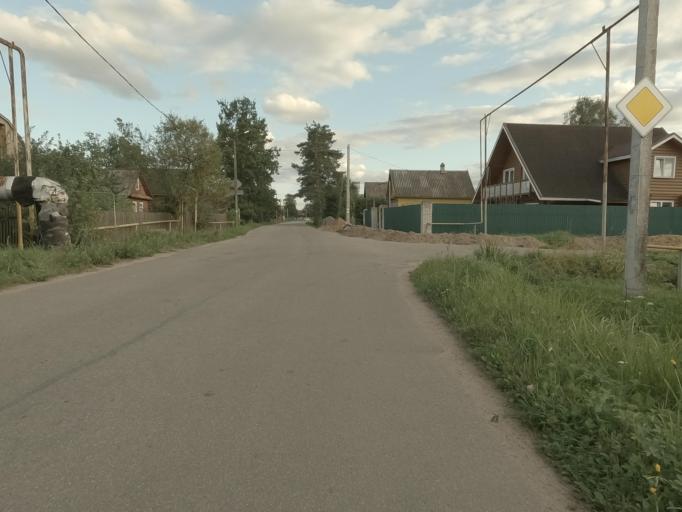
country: RU
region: Leningrad
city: Mga
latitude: 59.7591
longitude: 31.0765
